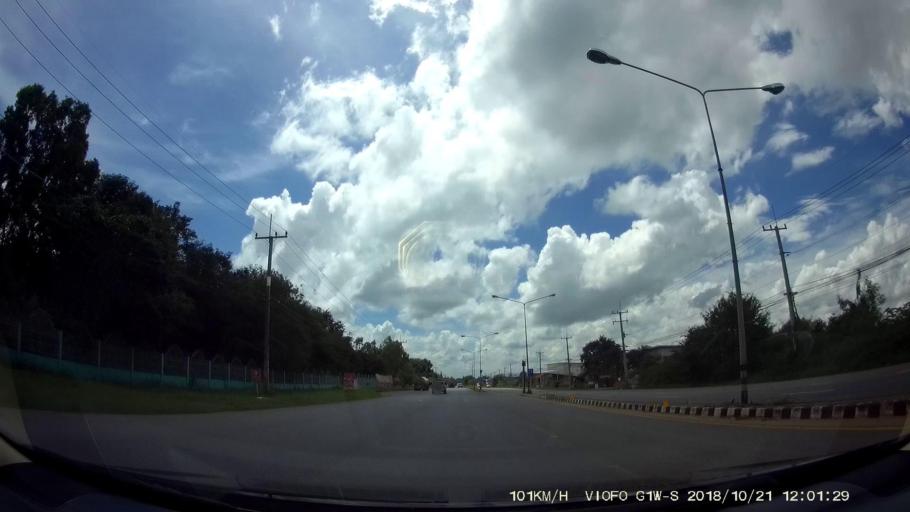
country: TH
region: Chaiyaphum
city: Chatturat
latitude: 15.5376
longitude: 101.8351
